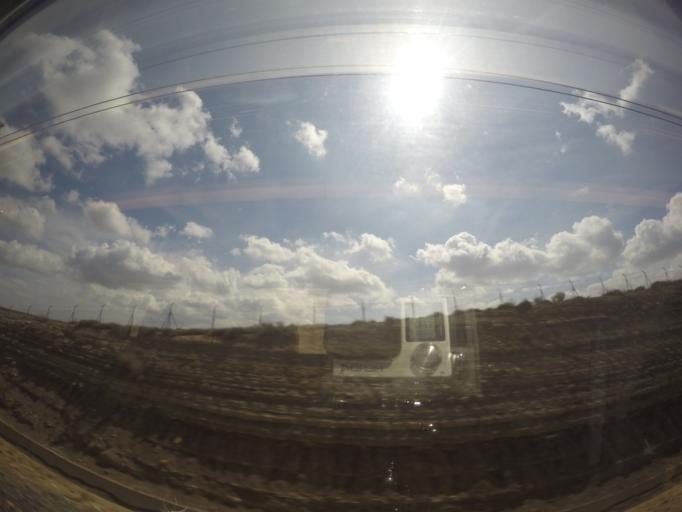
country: ES
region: Aragon
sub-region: Provincia de Huesca
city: Candasnos
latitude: 41.5717
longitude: 0.1062
